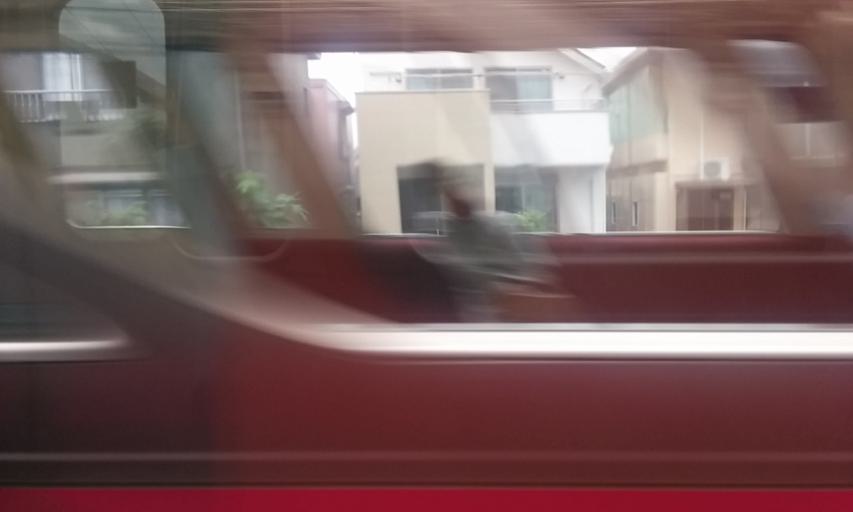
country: JP
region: Tokyo
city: Hino
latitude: 35.6617
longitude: 139.4005
